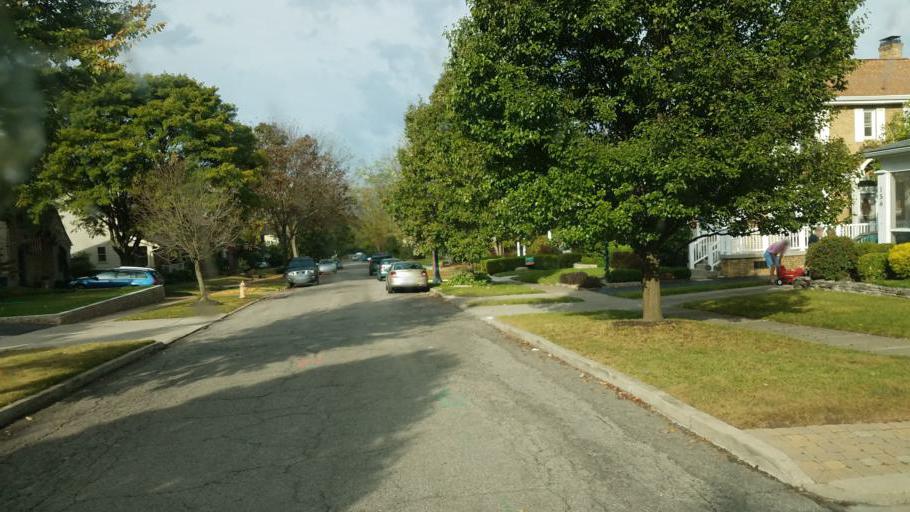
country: US
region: Ohio
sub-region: Franklin County
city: Worthington
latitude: 40.0383
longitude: -83.0127
